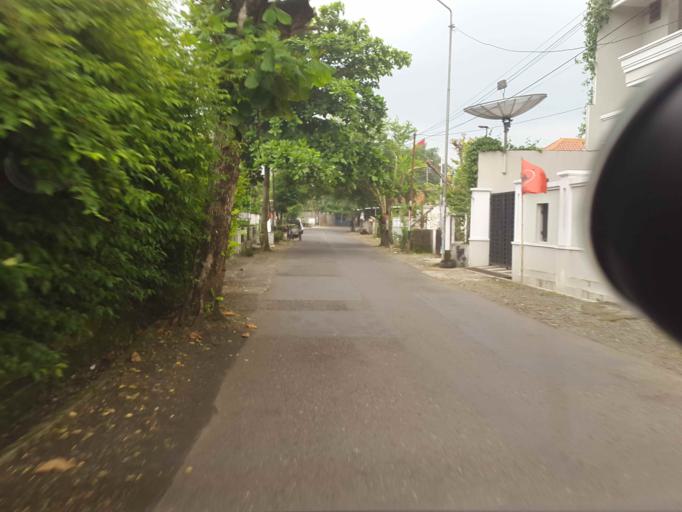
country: ID
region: Central Java
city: Purwokerto
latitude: -7.4230
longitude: 109.2376
